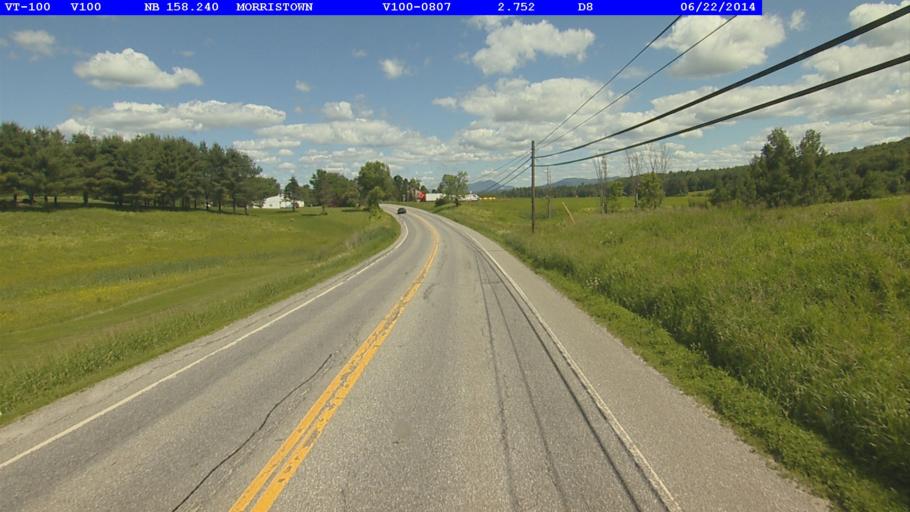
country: US
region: Vermont
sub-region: Lamoille County
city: Morristown
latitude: 44.5316
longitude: -72.6159
